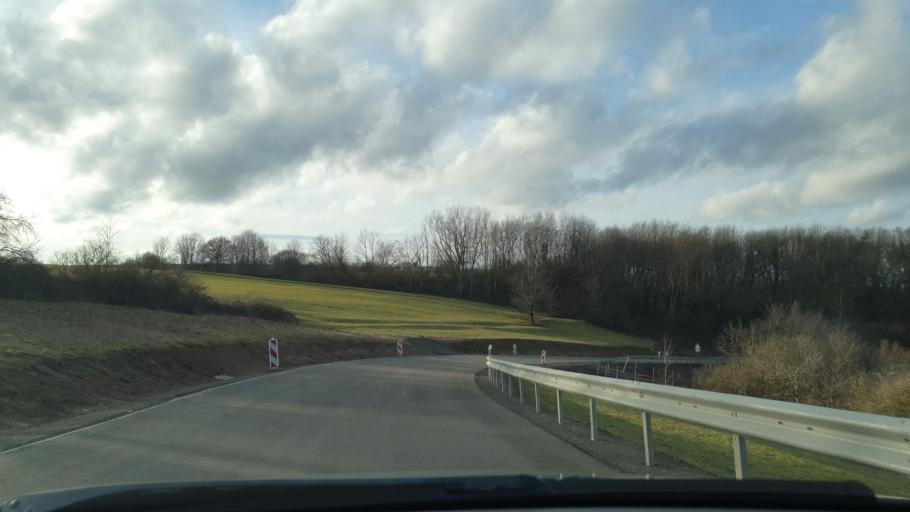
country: DE
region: Rheinland-Pfalz
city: Bann
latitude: 49.3705
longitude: 7.6189
